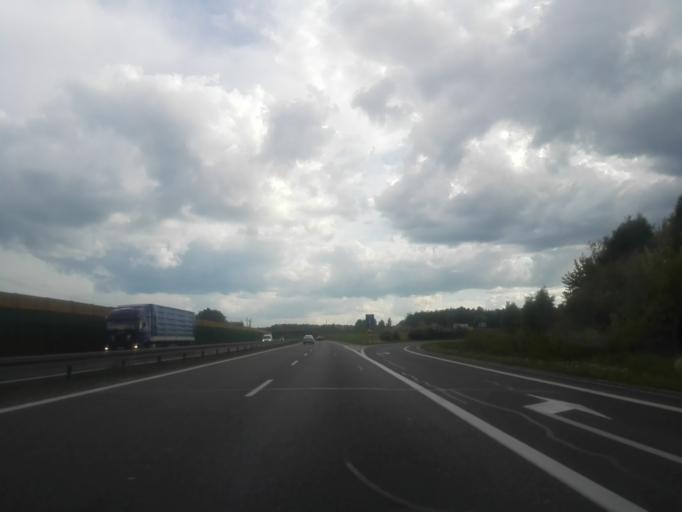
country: PL
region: Masovian Voivodeship
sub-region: Powiat ostrowski
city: Ostrow Mazowiecka
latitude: 52.8039
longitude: 21.8728
